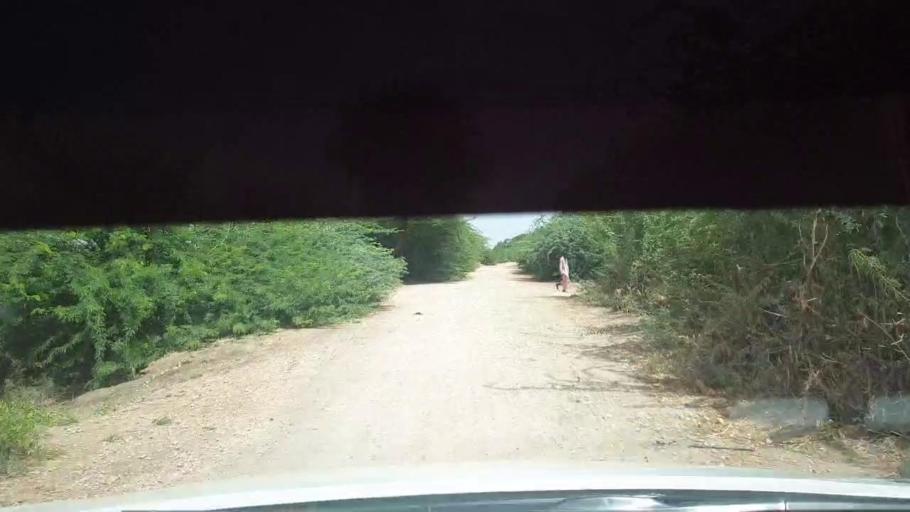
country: PK
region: Sindh
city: Kadhan
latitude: 24.5105
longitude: 68.9762
